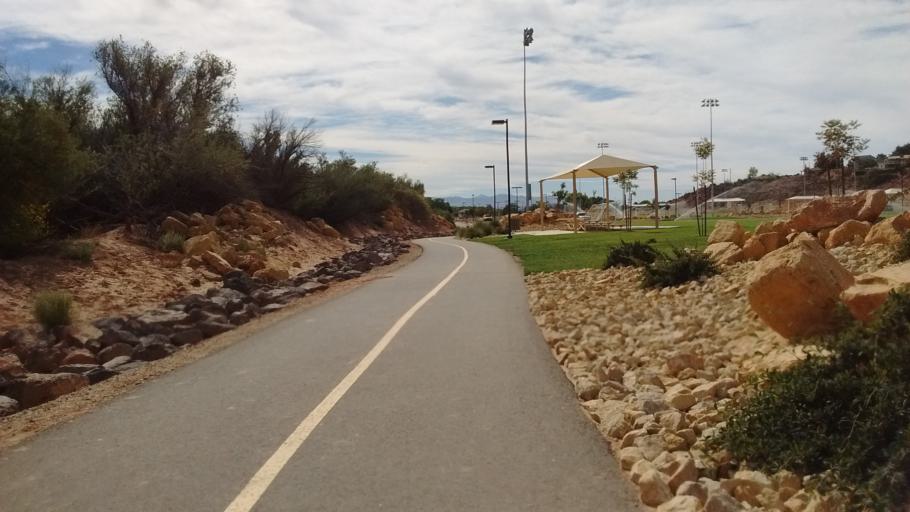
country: US
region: Utah
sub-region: Washington County
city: Washington
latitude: 37.1209
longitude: -113.4978
